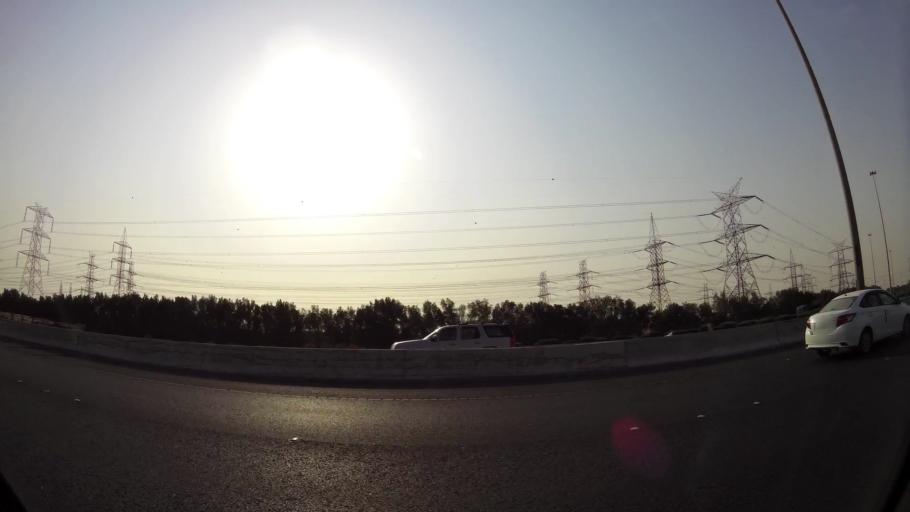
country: KW
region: Mubarak al Kabir
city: Sabah as Salim
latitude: 29.2606
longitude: 48.0439
